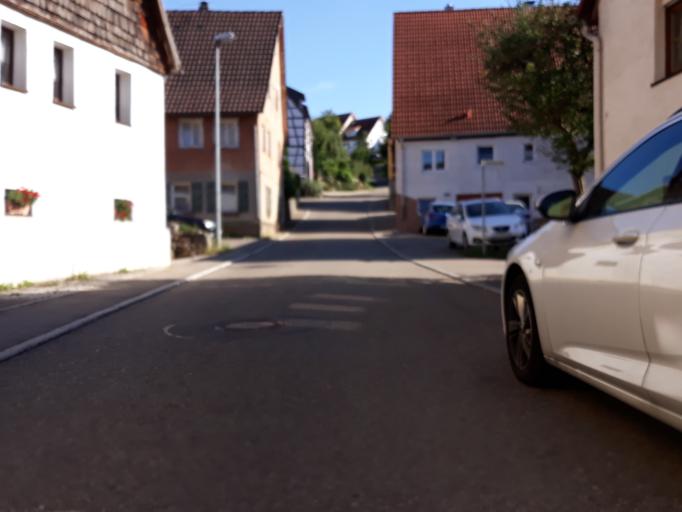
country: DE
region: Baden-Wuerttemberg
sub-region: Karlsruhe Region
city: Gechingen
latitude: 48.6940
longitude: 8.8316
